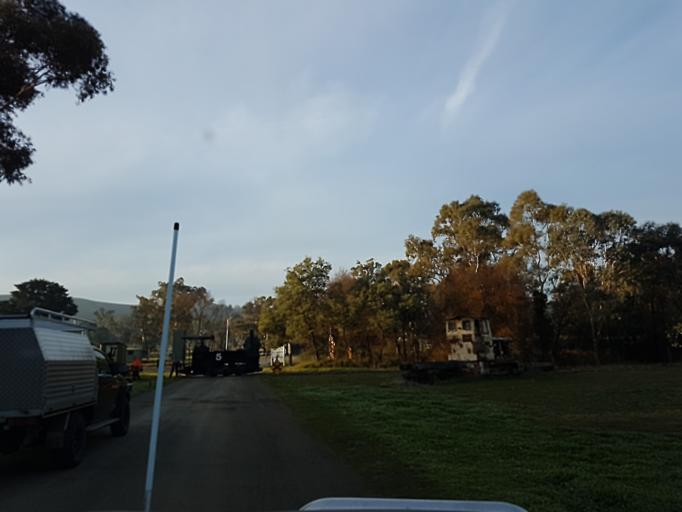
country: AU
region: Victoria
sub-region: Murrindindi
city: Alexandra
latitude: -37.1855
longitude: 145.7153
